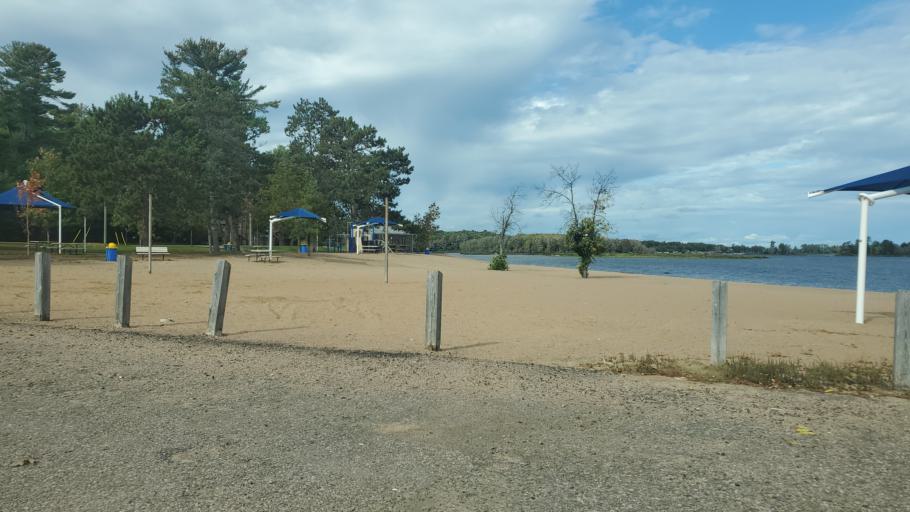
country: CA
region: Ontario
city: Petawawa
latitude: 45.9097
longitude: -77.2508
